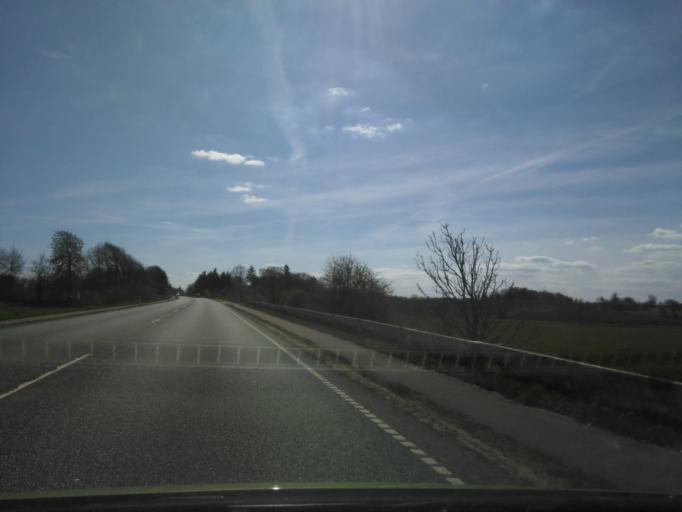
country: DK
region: Central Jutland
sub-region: Silkeborg Kommune
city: Kjellerup
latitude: 56.3436
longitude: 9.3495
